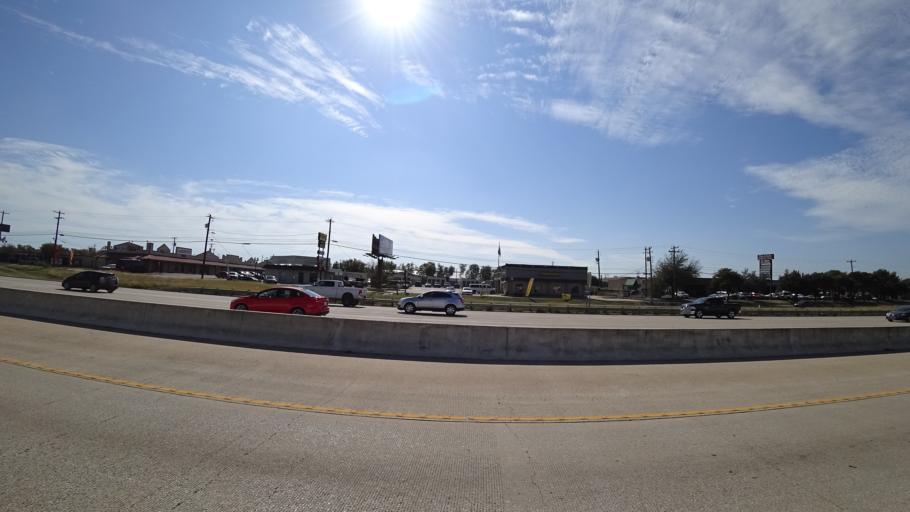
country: US
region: Texas
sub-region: Travis County
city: Austin
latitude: 30.2209
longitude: -97.7601
